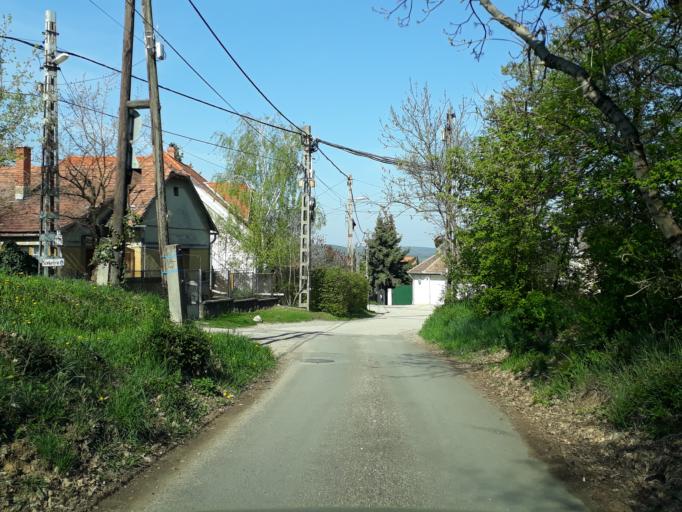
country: HU
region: Pest
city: Budakeszi
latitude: 47.5070
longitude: 18.9342
